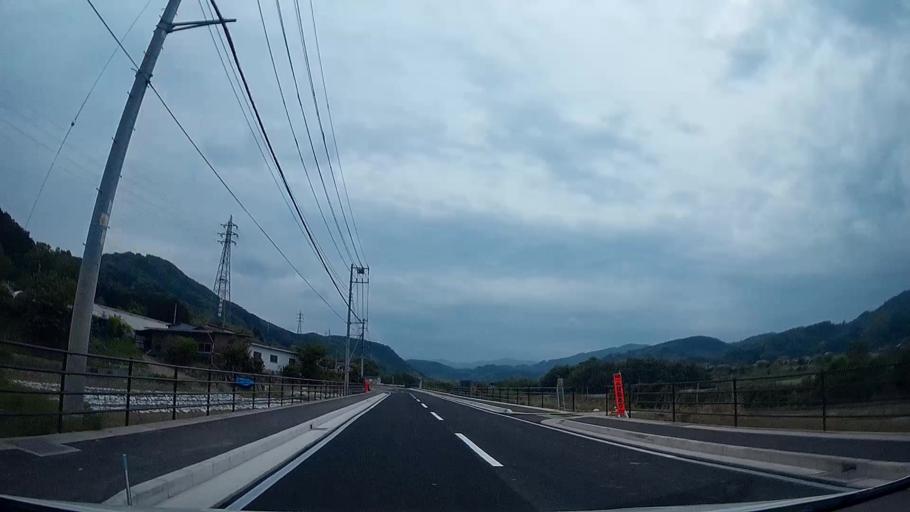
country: JP
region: Shizuoka
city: Ito
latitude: 34.9556
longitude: 138.9435
